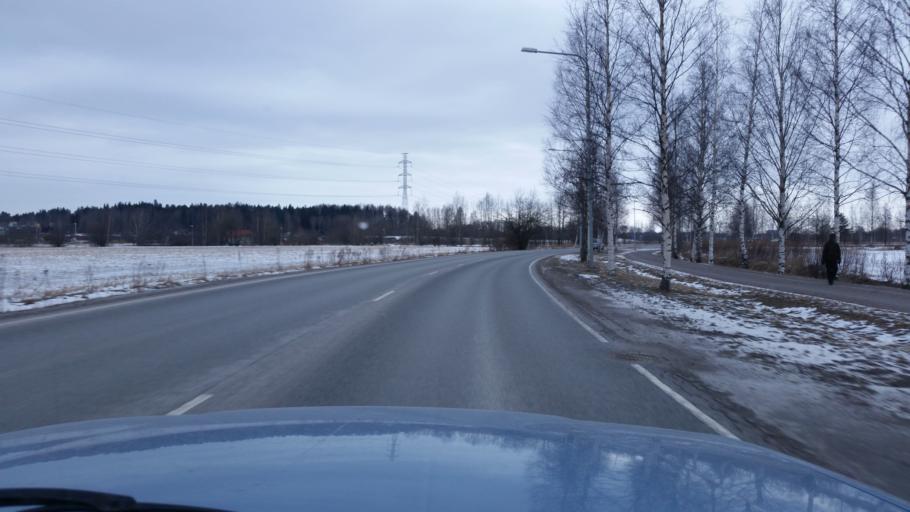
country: FI
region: Uusimaa
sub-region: Helsinki
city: Vantaa
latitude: 60.2451
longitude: 24.9771
